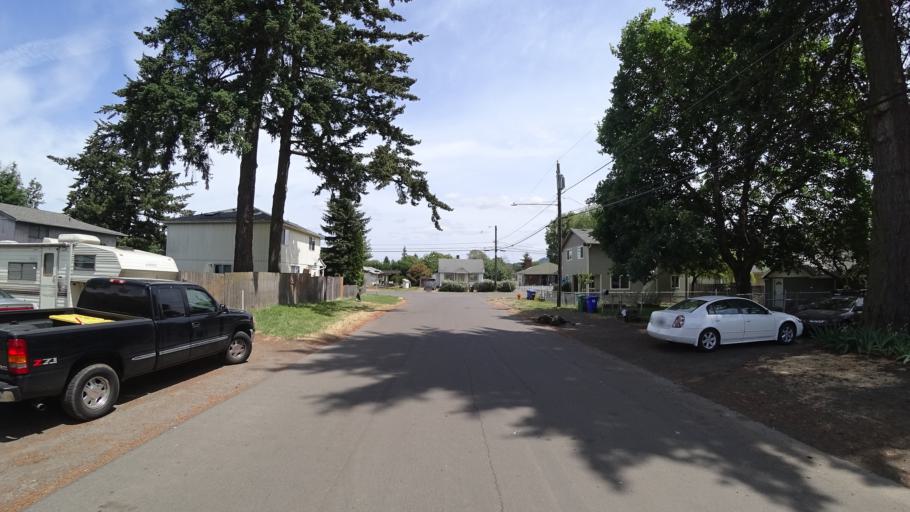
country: US
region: Oregon
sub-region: Multnomah County
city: Lents
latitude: 45.4665
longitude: -122.6002
